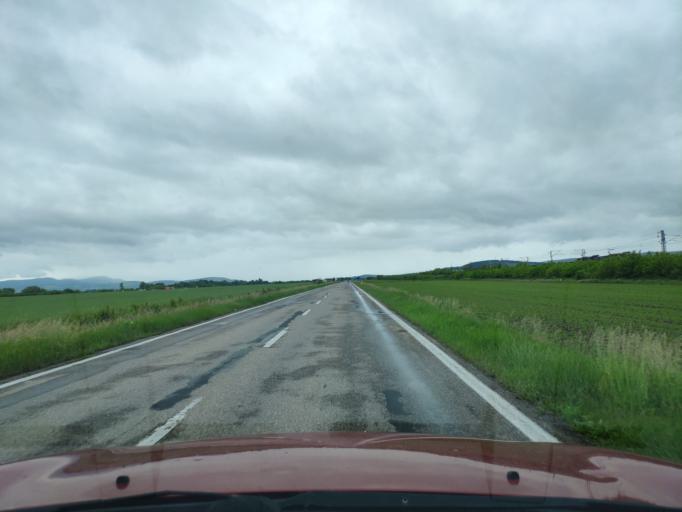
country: HU
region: Borsod-Abauj-Zemplen
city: Satoraljaujhely
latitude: 48.4192
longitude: 21.6631
